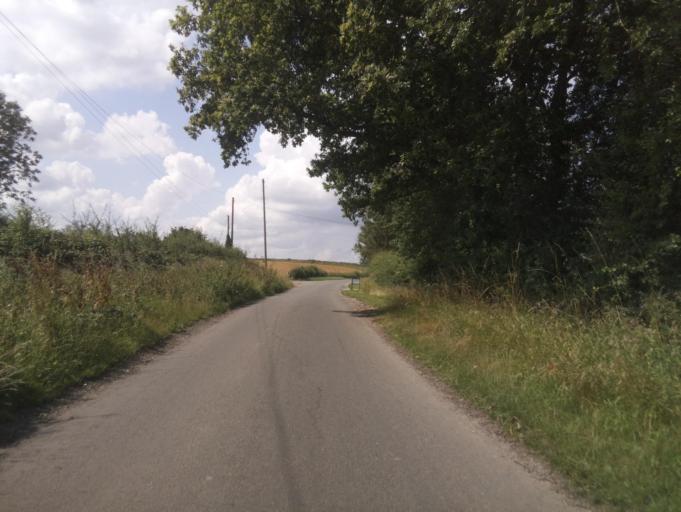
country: GB
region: England
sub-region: Wiltshire
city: Malmesbury
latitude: 51.5753
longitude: -2.1192
